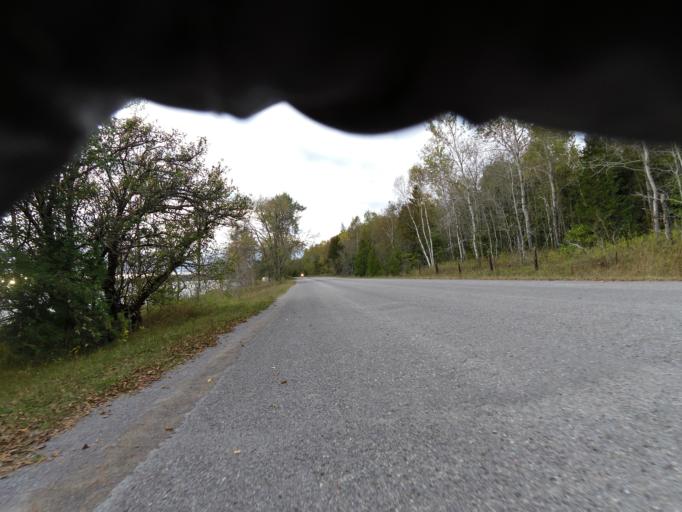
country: CA
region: Ontario
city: Cobourg
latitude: 43.9770
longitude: -77.9645
